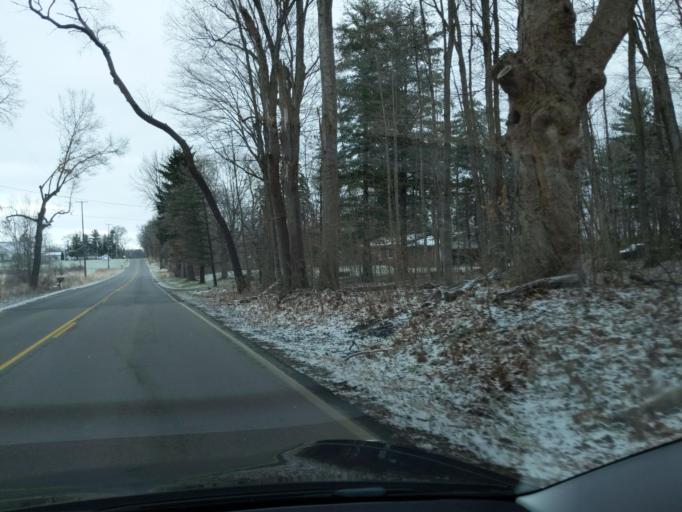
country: US
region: Michigan
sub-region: Jackson County
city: Spring Arbor
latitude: 42.2471
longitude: -84.5177
